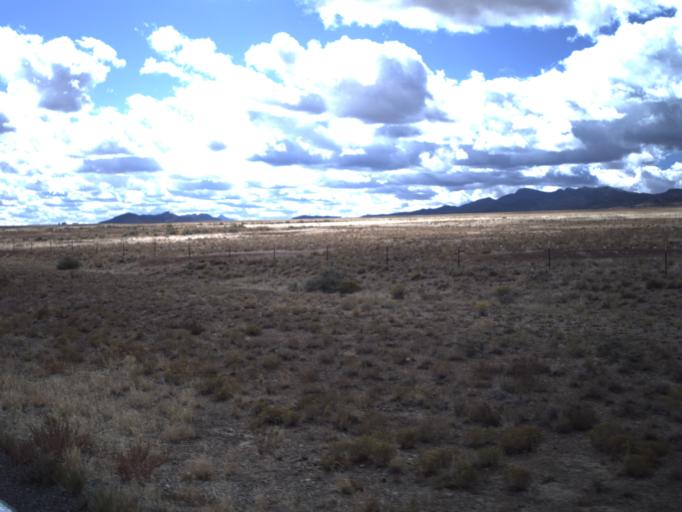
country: US
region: Utah
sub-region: Beaver County
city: Milford
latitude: 38.6703
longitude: -113.8844
